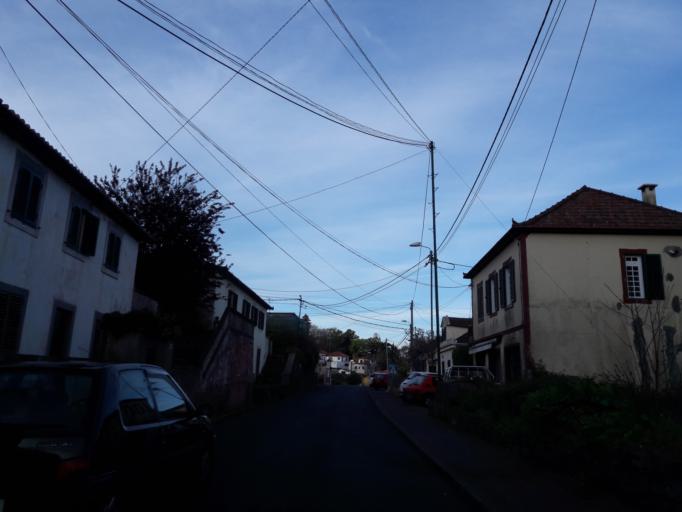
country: PT
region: Madeira
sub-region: Santa Cruz
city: Camacha
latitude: 32.6789
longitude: -16.8490
